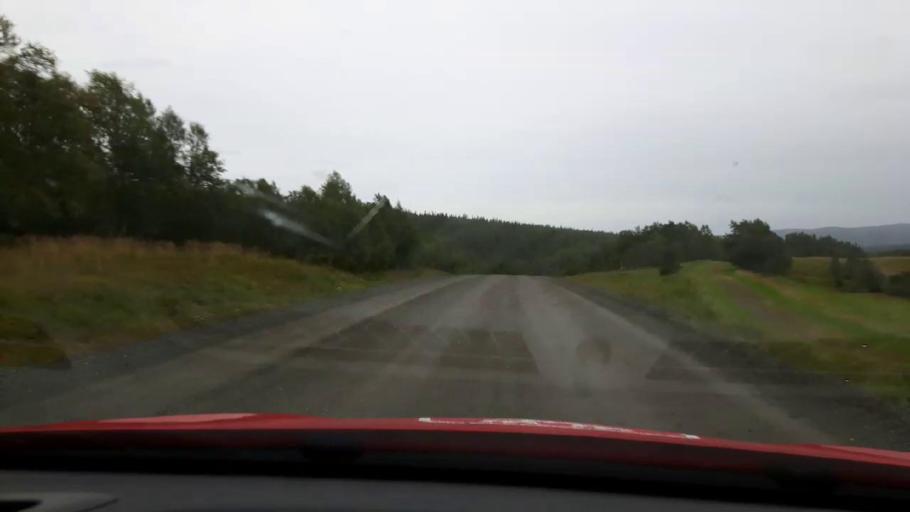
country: NO
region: Nord-Trondelag
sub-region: Meraker
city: Meraker
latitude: 63.5787
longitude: 12.2734
